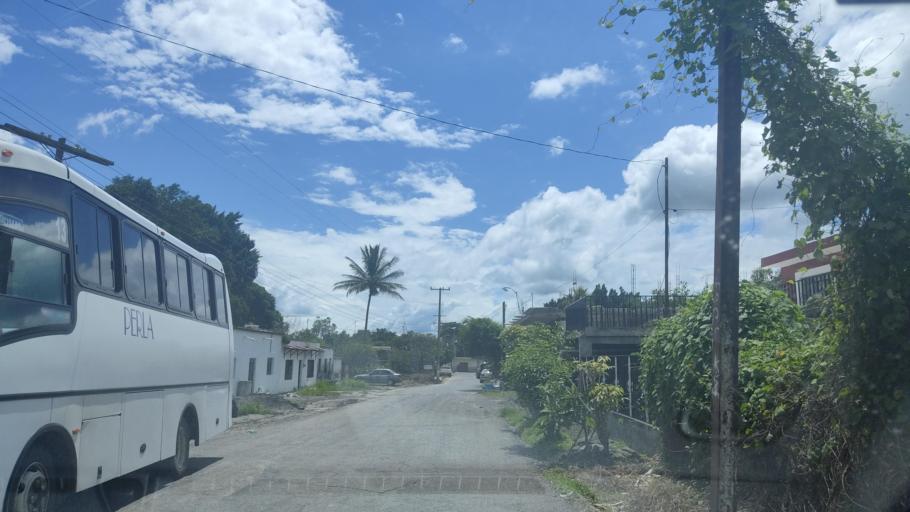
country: MX
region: Nayarit
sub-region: Ahuacatlan
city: Ahuacatlan
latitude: 21.1212
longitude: -104.6216
